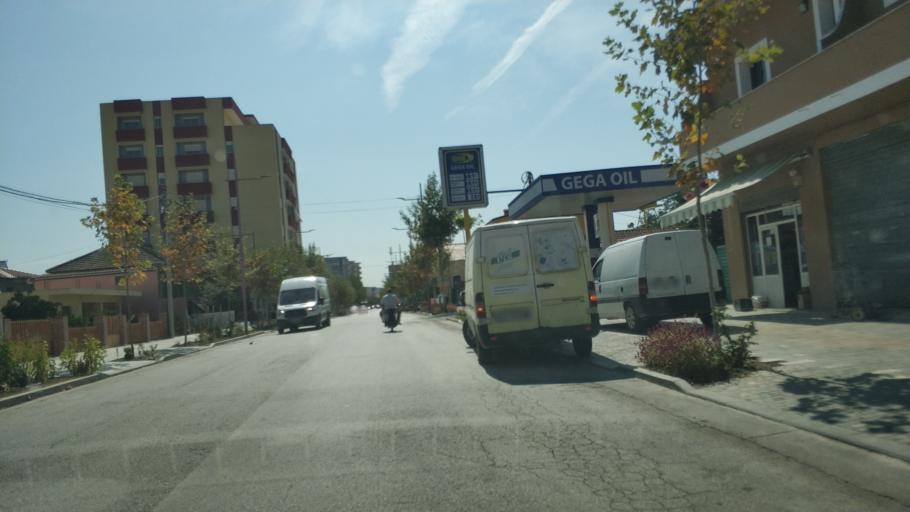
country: AL
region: Fier
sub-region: Rrethi i Lushnjes
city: Divjake
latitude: 40.9996
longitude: 19.5314
